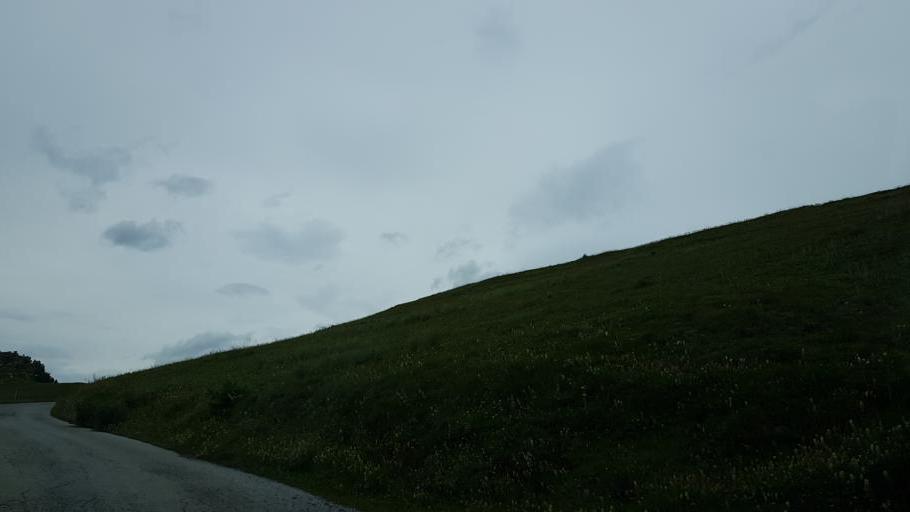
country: IT
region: Piedmont
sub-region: Provincia di Cuneo
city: Serre
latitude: 44.5489
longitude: 7.1204
